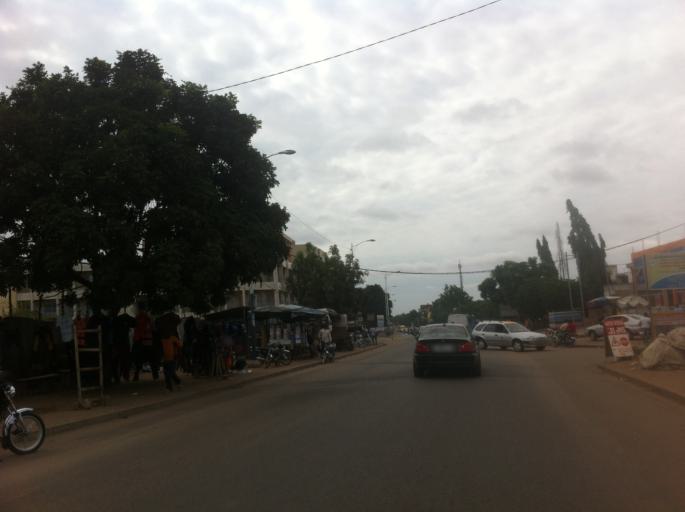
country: TG
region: Maritime
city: Lome
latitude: 6.1816
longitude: 1.1703
